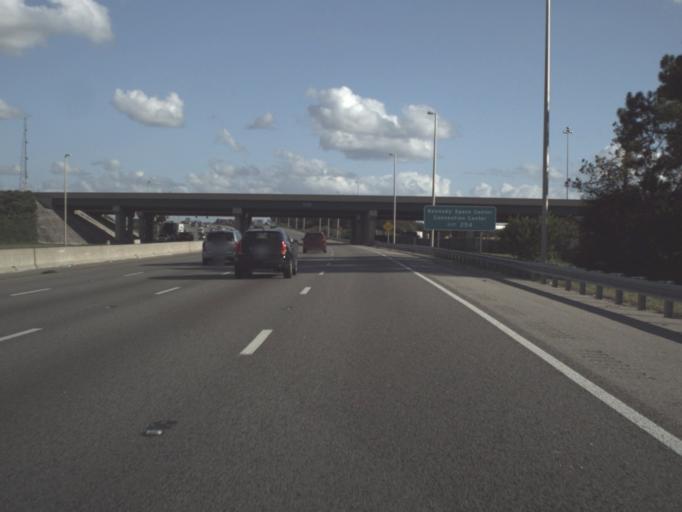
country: US
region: Florida
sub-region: Orange County
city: Sky Lake
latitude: 28.4345
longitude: -81.4102
